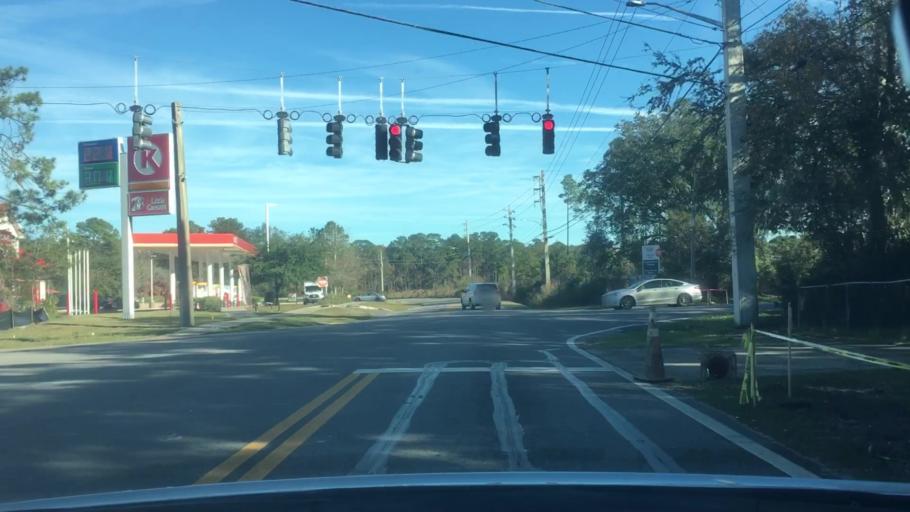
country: US
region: Florida
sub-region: Nassau County
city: Yulee
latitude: 30.5037
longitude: -81.5784
